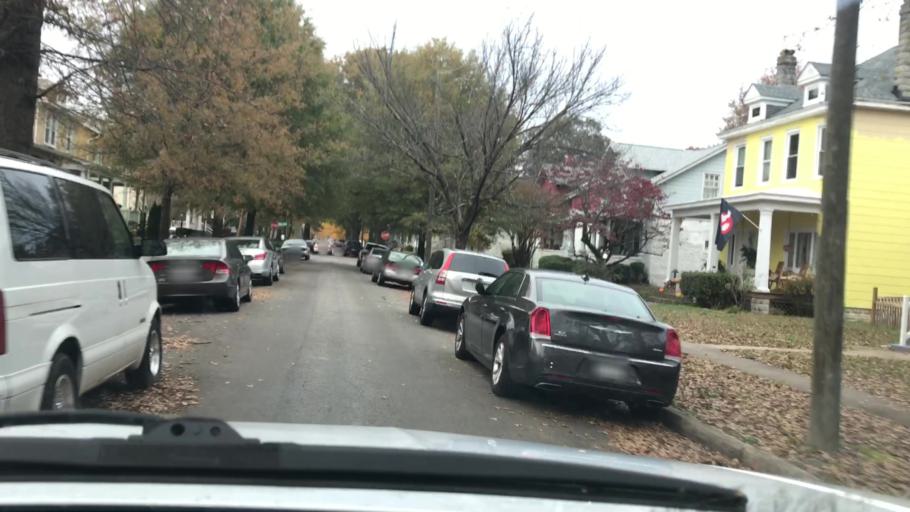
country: US
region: Virginia
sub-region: City of Richmond
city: Richmond
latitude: 37.5696
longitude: -77.4388
